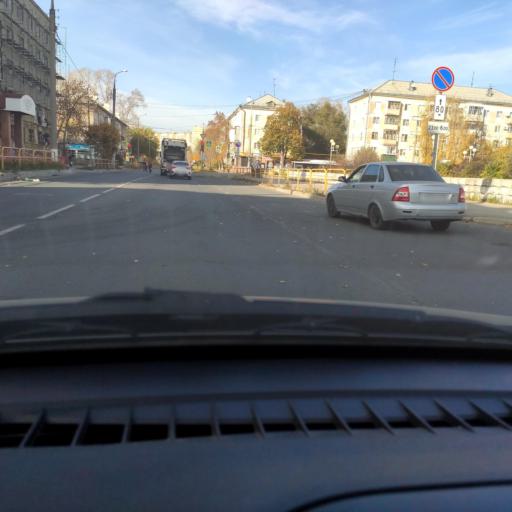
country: RU
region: Samara
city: Tol'yatti
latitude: 53.5033
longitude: 49.4005
